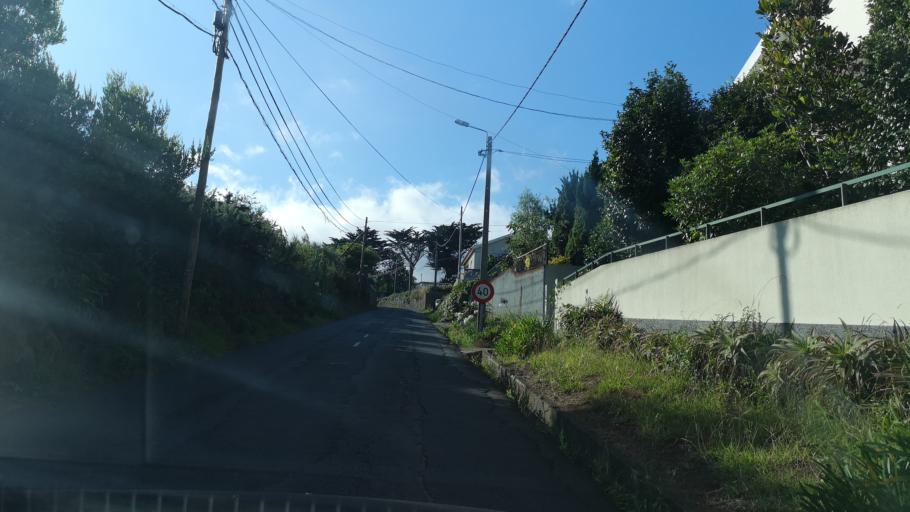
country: PT
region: Madeira
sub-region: Santa Cruz
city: Camacha
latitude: 32.6689
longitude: -16.8430
